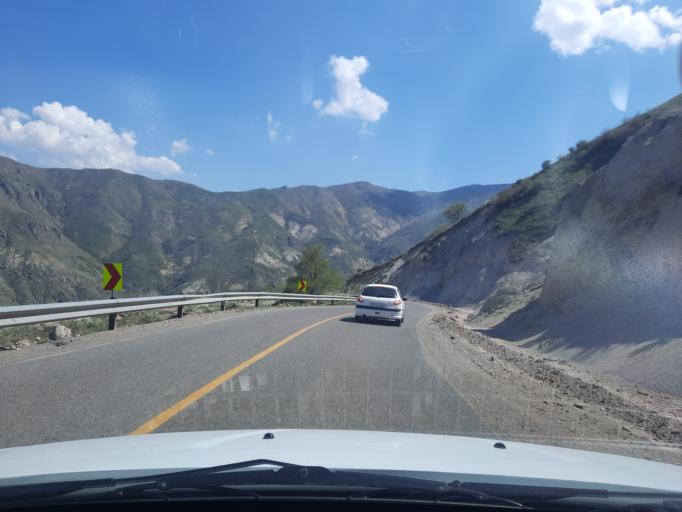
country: IR
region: Qazvin
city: Qazvin
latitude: 36.4126
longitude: 50.2432
